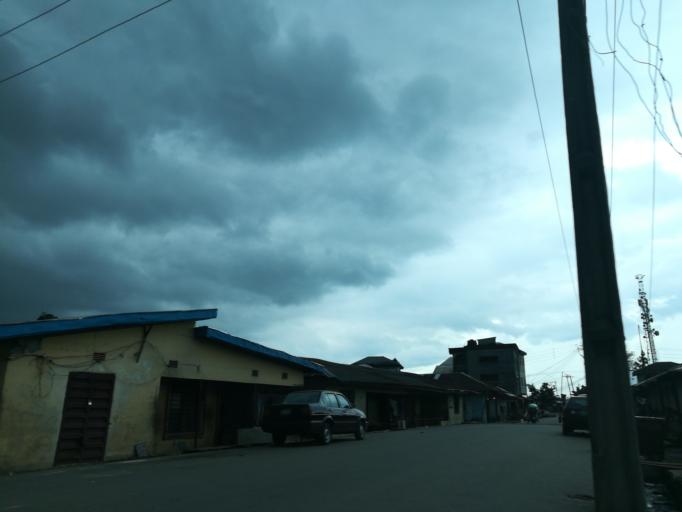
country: NG
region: Rivers
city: Port Harcourt
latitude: 4.8019
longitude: 6.9872
